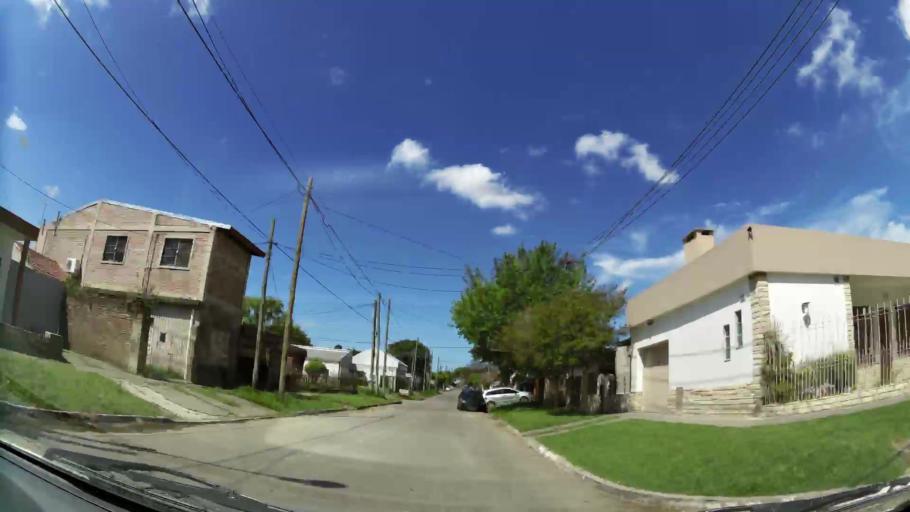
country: AR
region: Buenos Aires
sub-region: Partido de Quilmes
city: Quilmes
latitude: -34.8125
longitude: -58.2675
